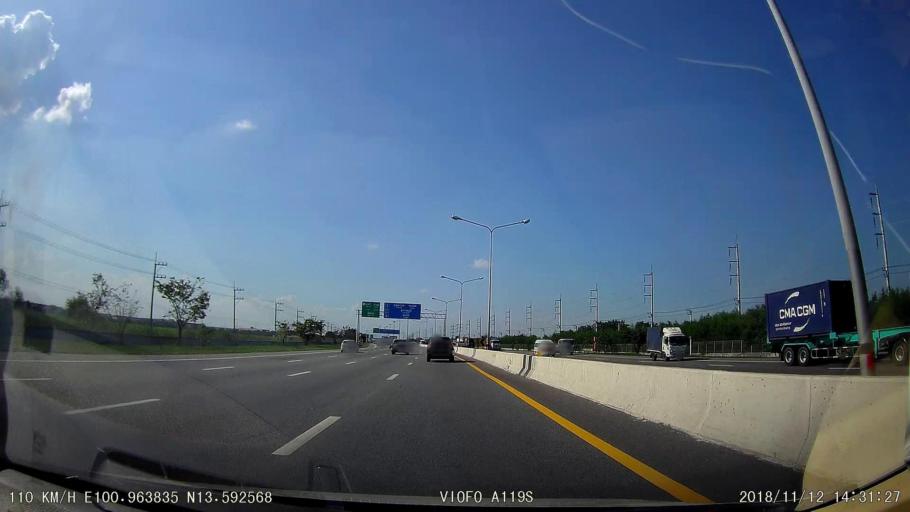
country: TH
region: Chachoengsao
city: Bang Pakong
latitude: 13.5927
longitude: 100.9637
